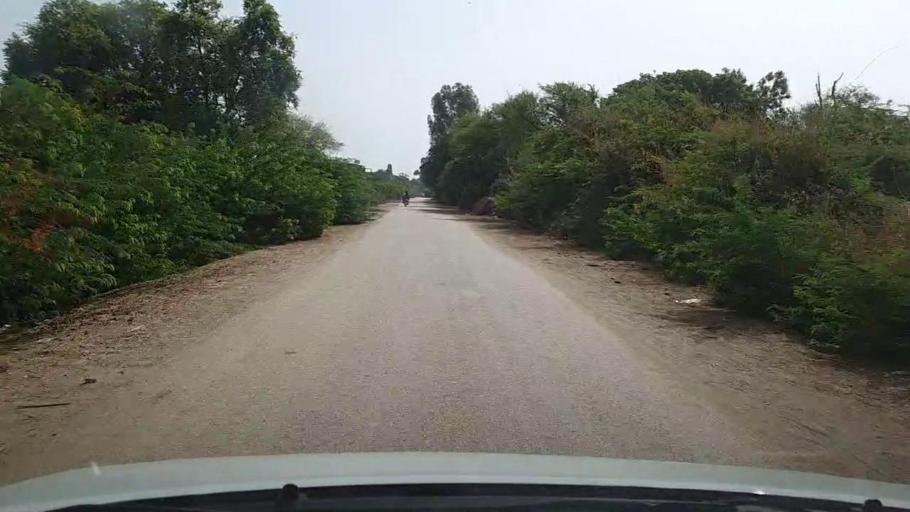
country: PK
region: Sindh
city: Mehar
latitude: 27.1260
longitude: 67.8625
